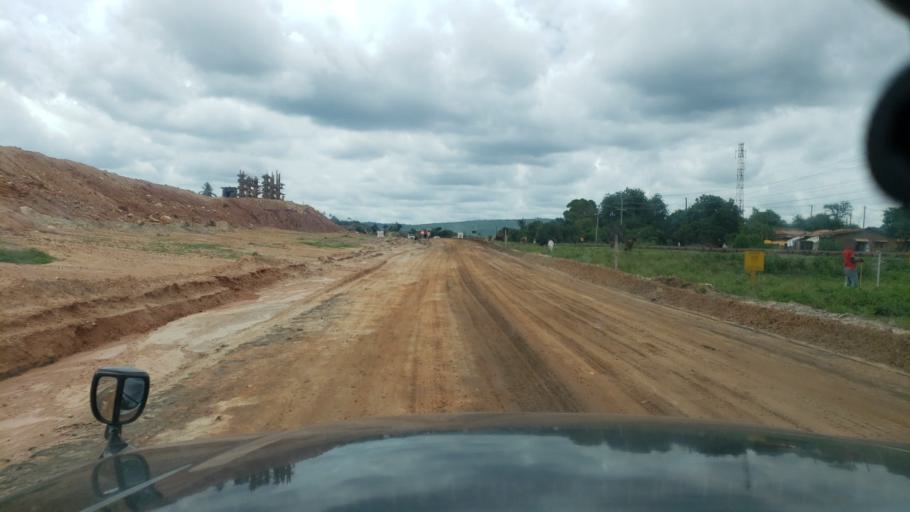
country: TZ
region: Pwani
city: Kisarawe
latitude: -6.8852
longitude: 39.1448
